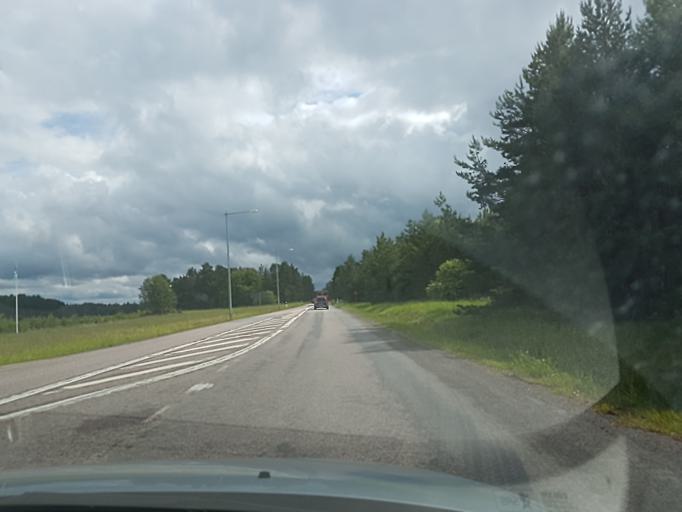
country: SE
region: Uppsala
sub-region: Osthammars Kommun
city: OEsthammar
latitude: 60.2492
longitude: 18.3475
